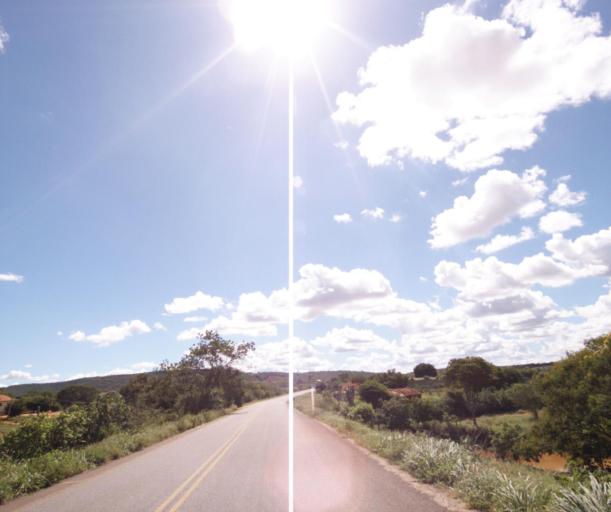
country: BR
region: Bahia
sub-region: Caetite
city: Caetite
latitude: -14.1723
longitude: -42.1907
